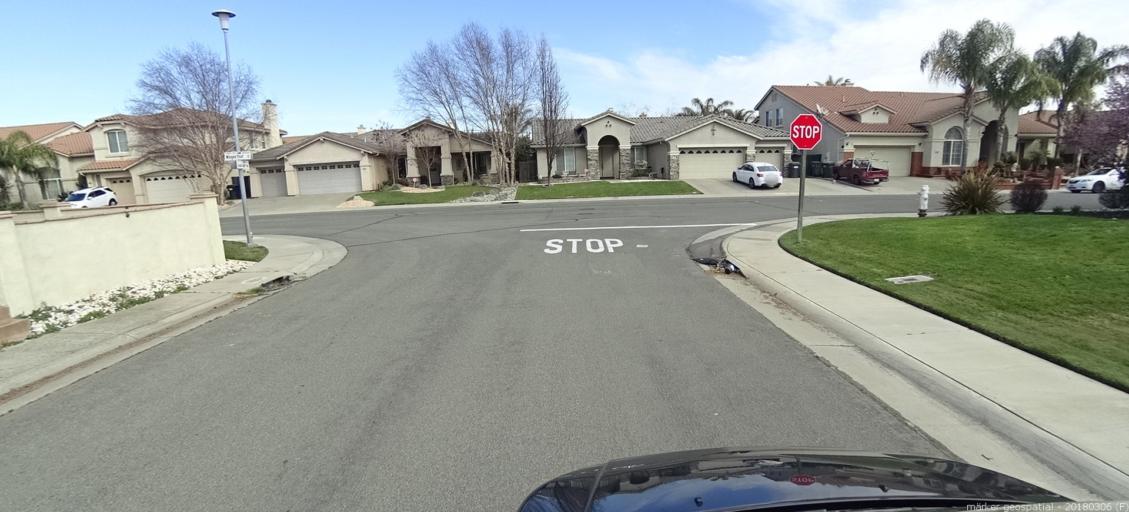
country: US
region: California
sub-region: Sacramento County
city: Vineyard
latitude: 38.4691
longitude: -121.3189
